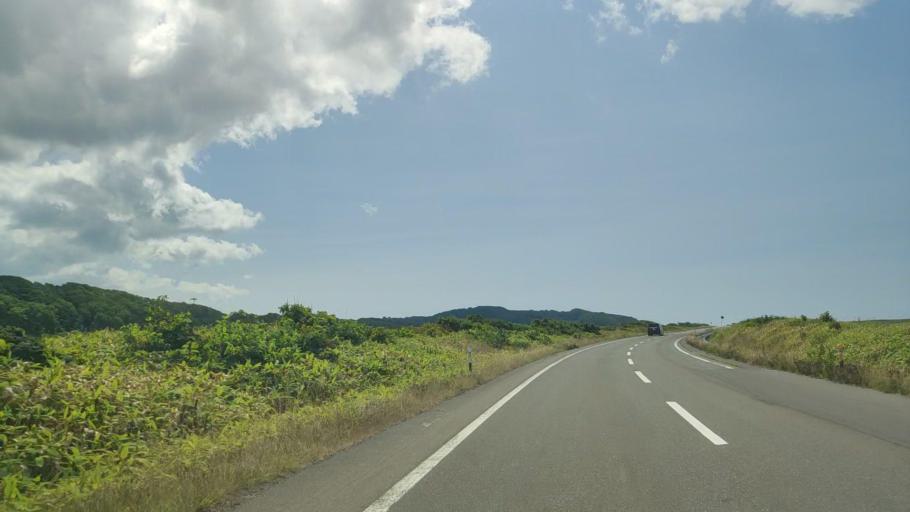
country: JP
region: Hokkaido
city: Wakkanai
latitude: 45.2546
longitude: 141.5952
